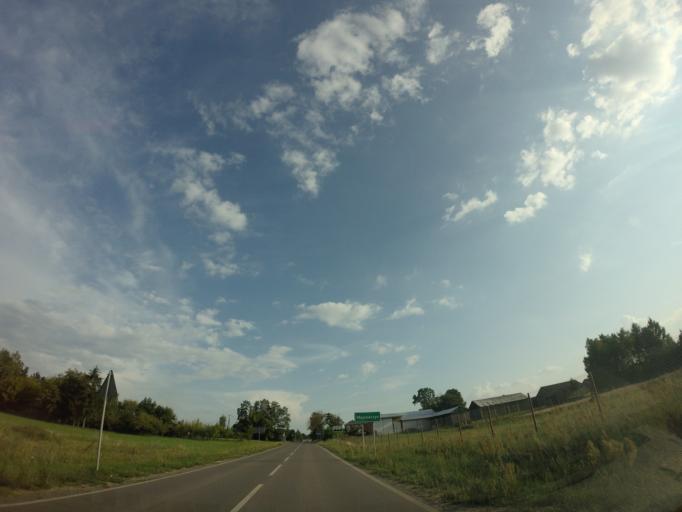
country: PL
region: Lublin Voivodeship
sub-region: Powiat lubartowski
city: Michow
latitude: 51.5530
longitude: 22.2990
